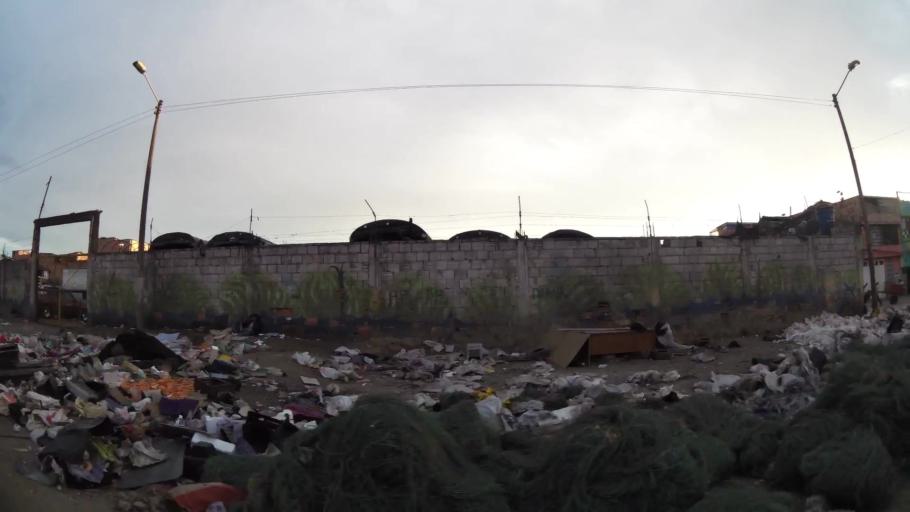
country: CO
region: Cundinamarca
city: Soacha
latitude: 4.6309
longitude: -74.1645
